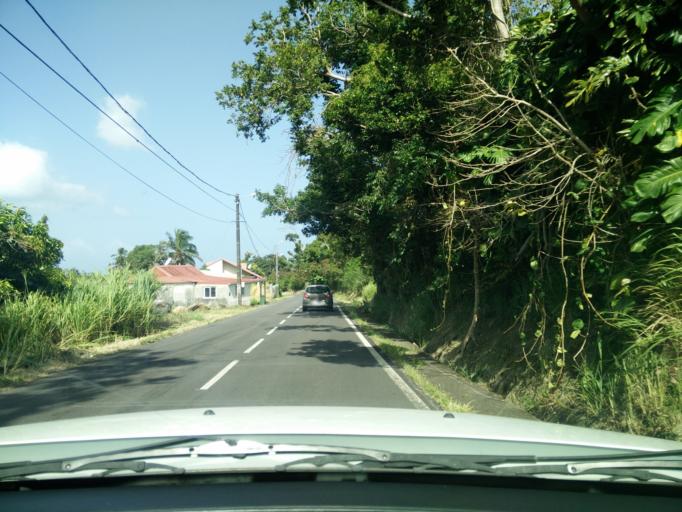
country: GP
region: Guadeloupe
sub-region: Guadeloupe
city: Gourbeyre
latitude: 15.9959
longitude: -61.7038
